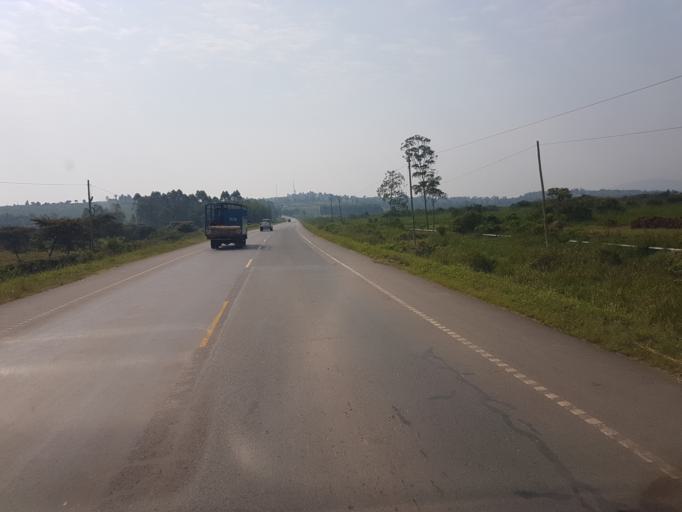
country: UG
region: Western Region
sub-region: Mbarara District
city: Bwizibwera
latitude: -0.6423
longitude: 30.5784
